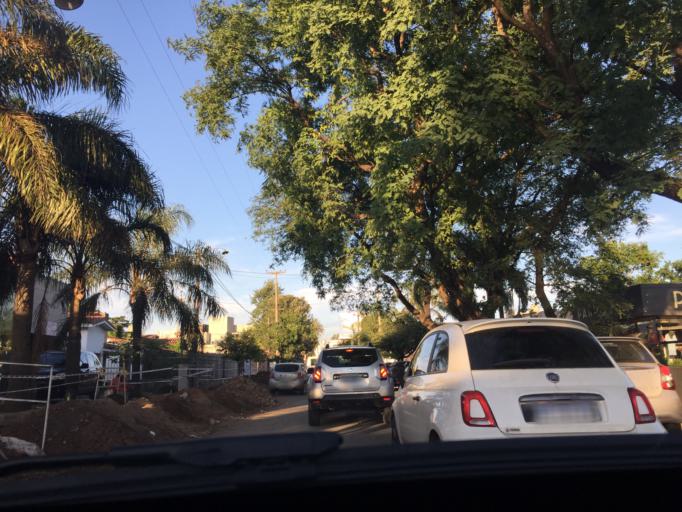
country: AR
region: Cordoba
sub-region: Departamento de Capital
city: Cordoba
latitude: -31.3681
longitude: -64.2350
